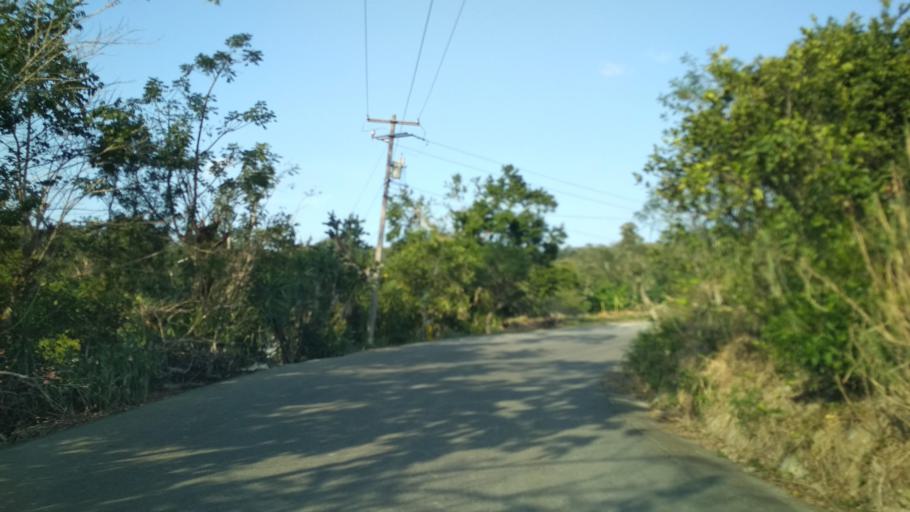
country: MX
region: Veracruz
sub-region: Poza Rica de Hidalgo
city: Arroyo del Maiz Uno
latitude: 20.4868
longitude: -97.3862
